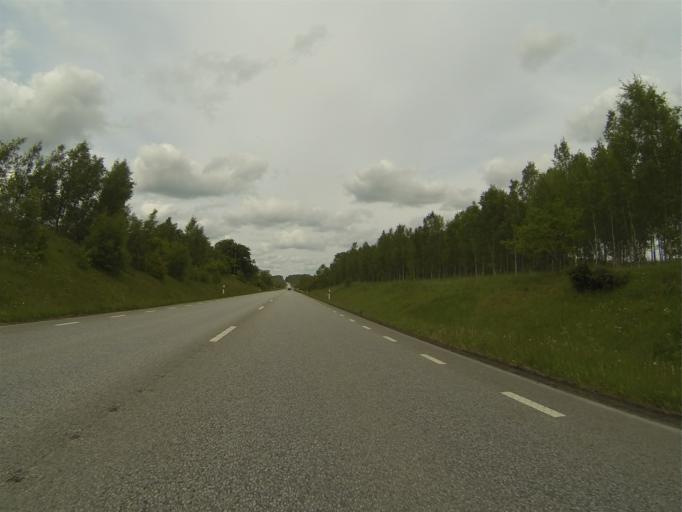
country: SE
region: Skane
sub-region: Sjobo Kommun
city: Sjoebo
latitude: 55.6456
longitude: 13.6905
